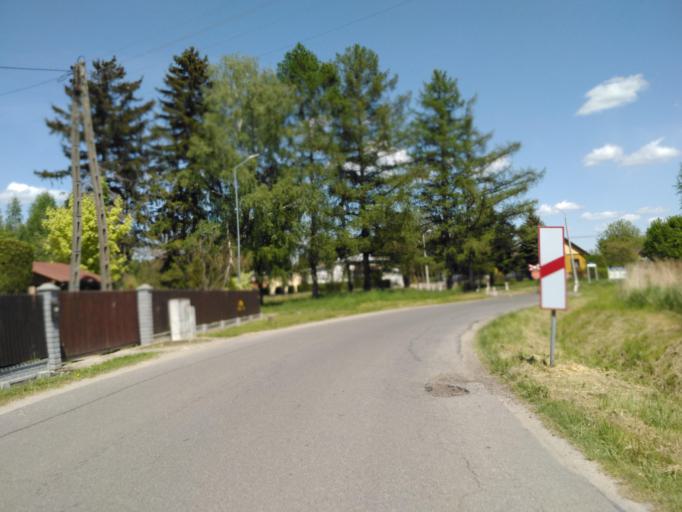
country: PL
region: Subcarpathian Voivodeship
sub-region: Powiat krosnienski
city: Jedlicze
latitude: 49.7091
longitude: 21.6962
